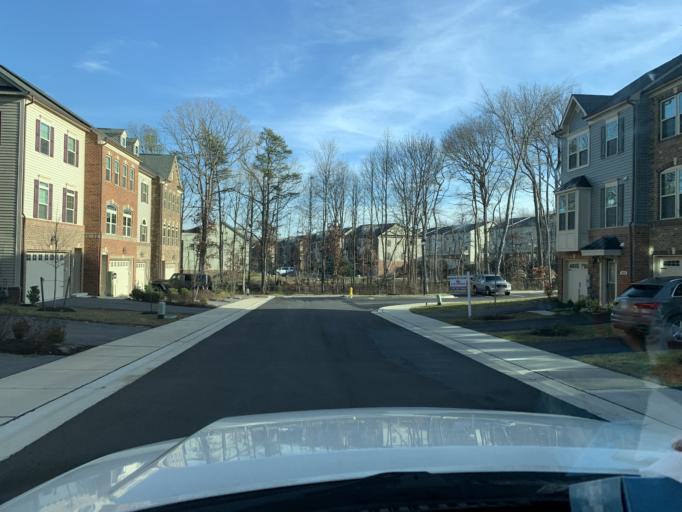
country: US
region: Maryland
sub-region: Anne Arundel County
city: Fort Meade
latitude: 39.1315
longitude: -76.7492
